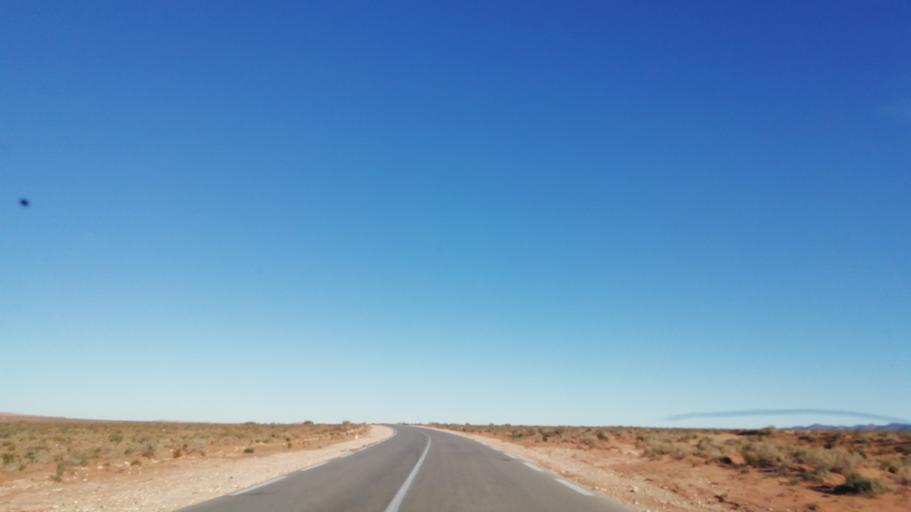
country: DZ
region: El Bayadh
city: El Abiodh Sidi Cheikh
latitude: 33.1119
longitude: 0.2589
